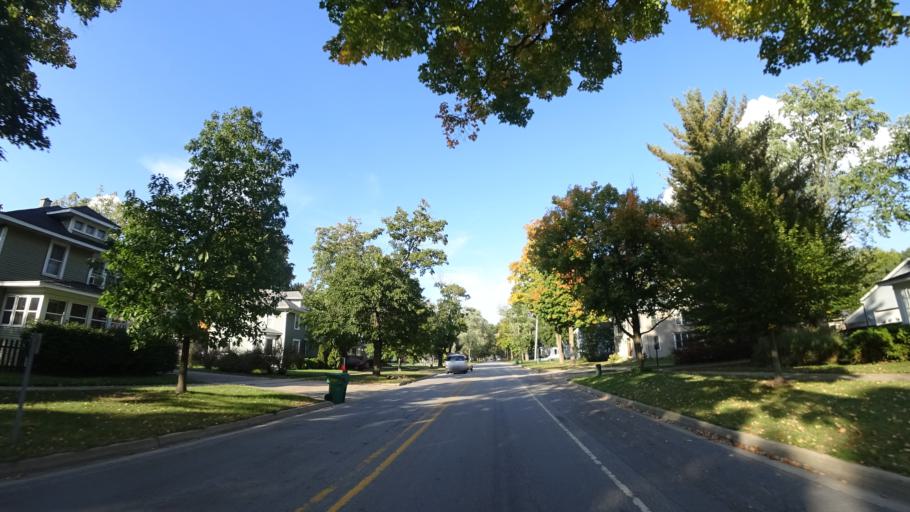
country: US
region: Michigan
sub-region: Saint Joseph County
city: Three Rivers
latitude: 41.9517
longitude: -85.6301
